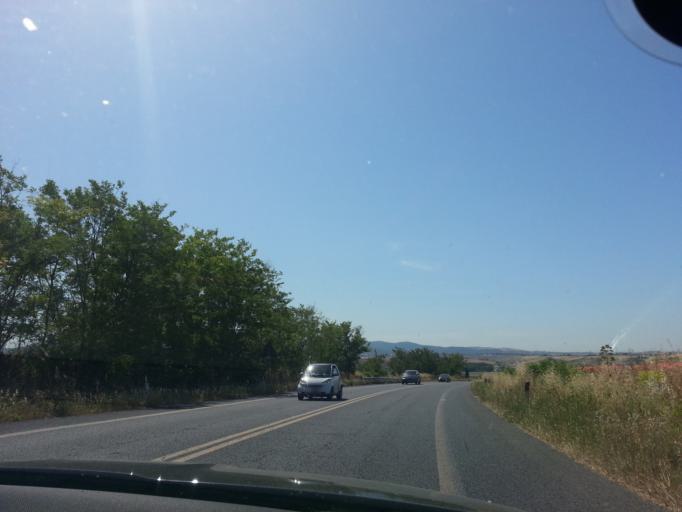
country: IT
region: Latium
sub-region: Provincia di Viterbo
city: Tarquinia
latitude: 42.2083
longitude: 11.7832
